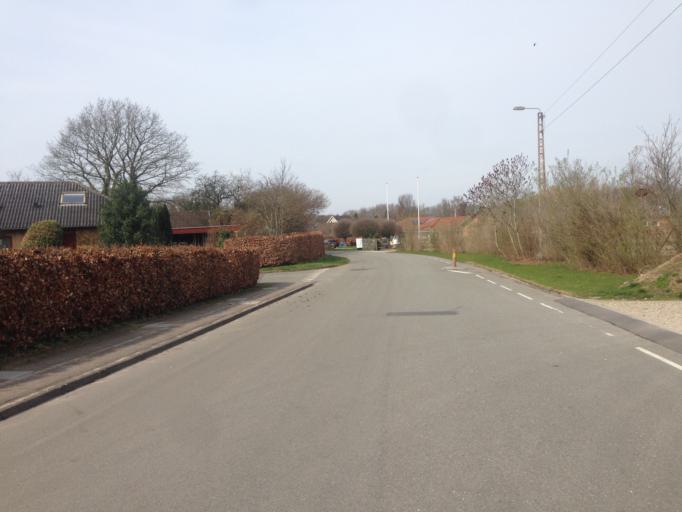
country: DK
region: South Denmark
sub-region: Sonderborg Kommune
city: Broager
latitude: 54.8916
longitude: 9.6561
